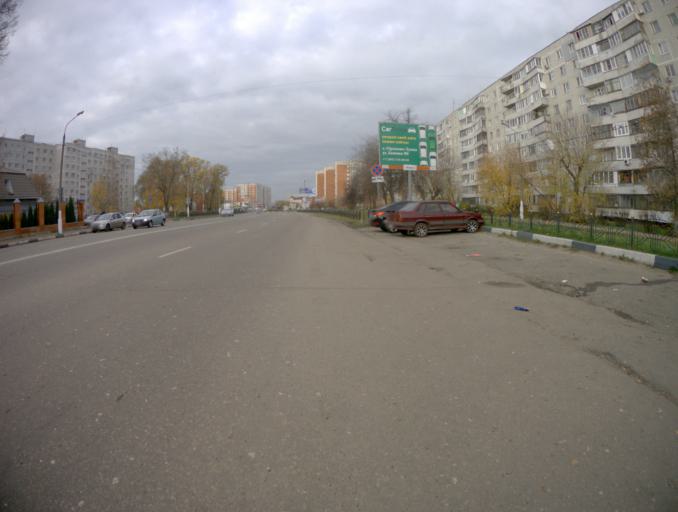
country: RU
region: Moskovskaya
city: Orekhovo-Zuyevo
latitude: 55.8082
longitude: 38.9581
